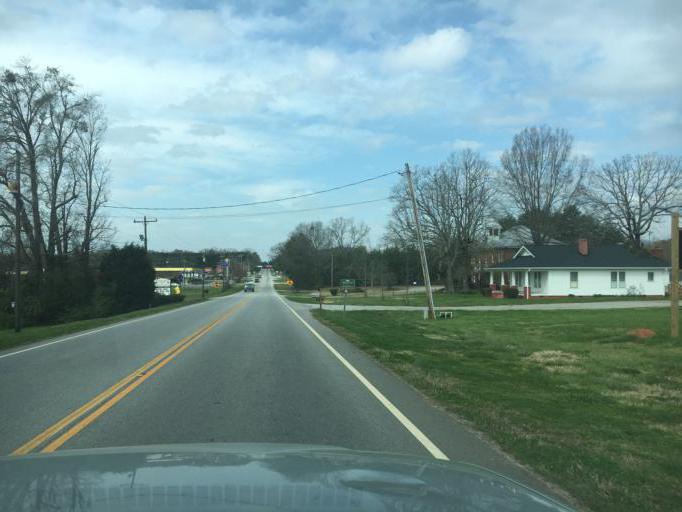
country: US
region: South Carolina
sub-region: Spartanburg County
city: Landrum
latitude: 35.1153
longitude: -82.2216
